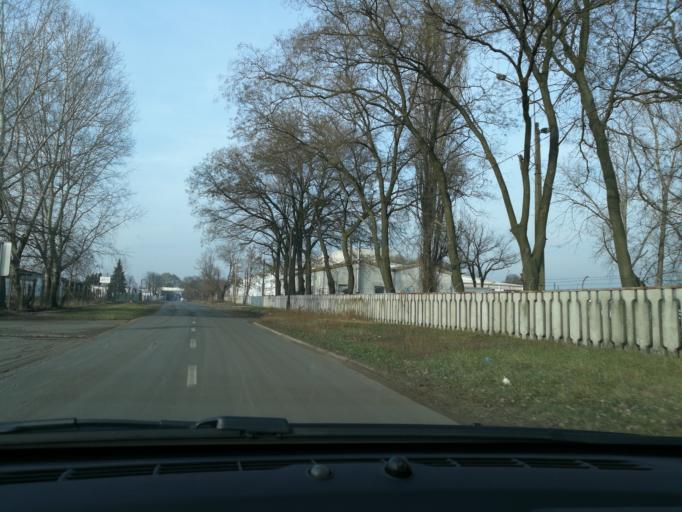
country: HU
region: Szabolcs-Szatmar-Bereg
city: Nyiregyhaza
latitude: 47.9466
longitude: 21.7024
